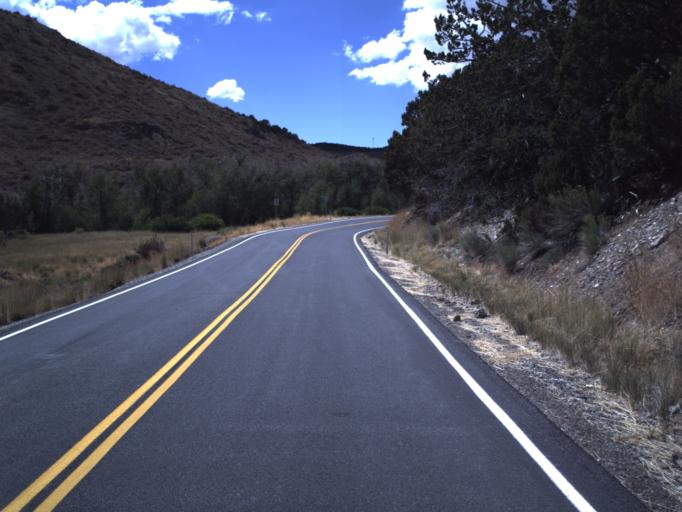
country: US
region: Utah
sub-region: Tooele County
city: Grantsville
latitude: 40.3419
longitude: -112.5401
